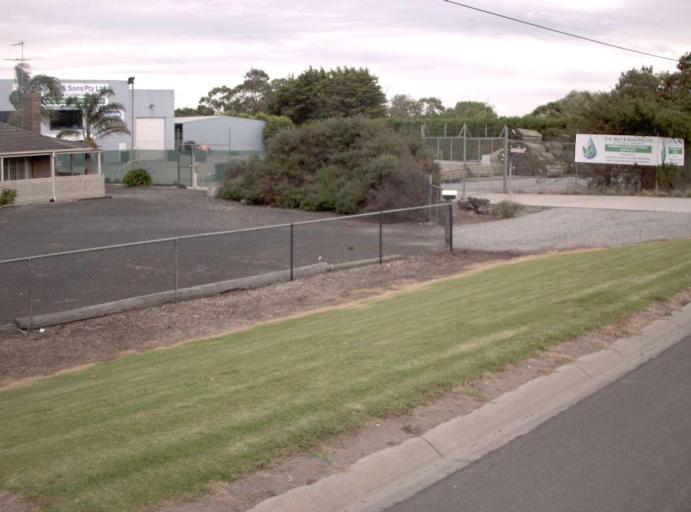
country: AU
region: Victoria
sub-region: Casey
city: Junction Village
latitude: -38.1557
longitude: 145.3174
